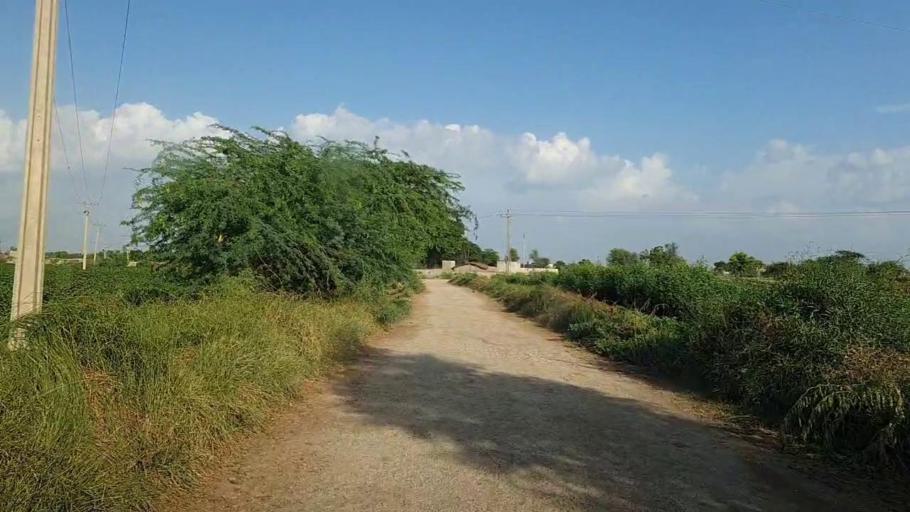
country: PK
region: Sindh
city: Hingorja
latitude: 27.0945
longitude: 68.3635
